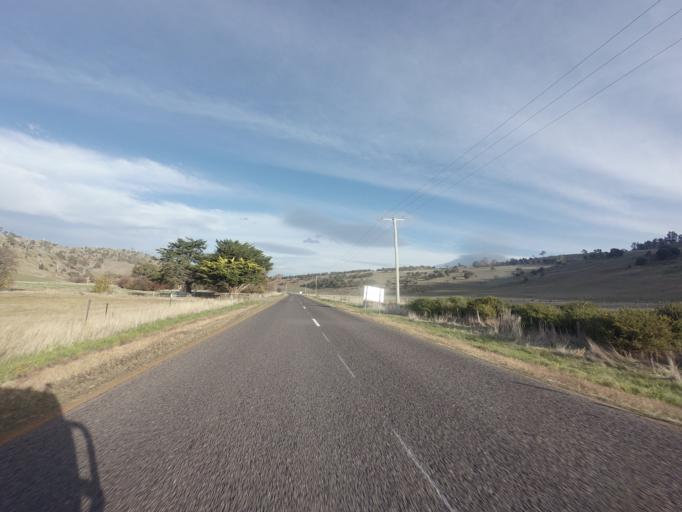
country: AU
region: Tasmania
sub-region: Brighton
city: Bridgewater
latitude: -42.4318
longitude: 147.1433
